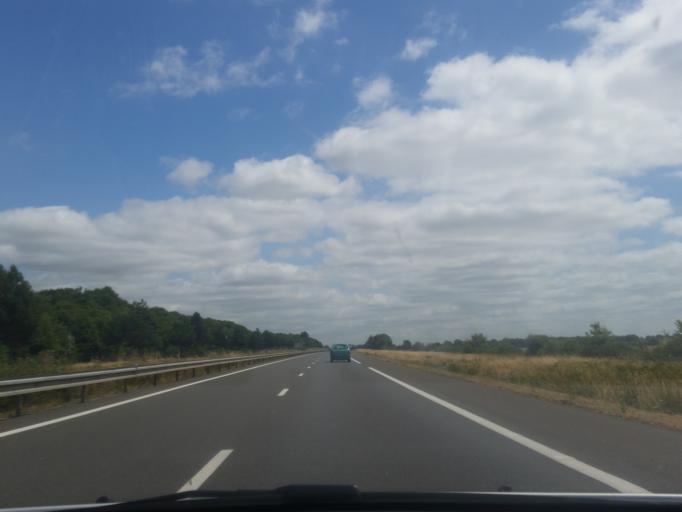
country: FR
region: Pays de la Loire
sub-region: Departement de Maine-et-Loire
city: Saint-Georges-sur-Loire
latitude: 47.4412
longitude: -0.7517
